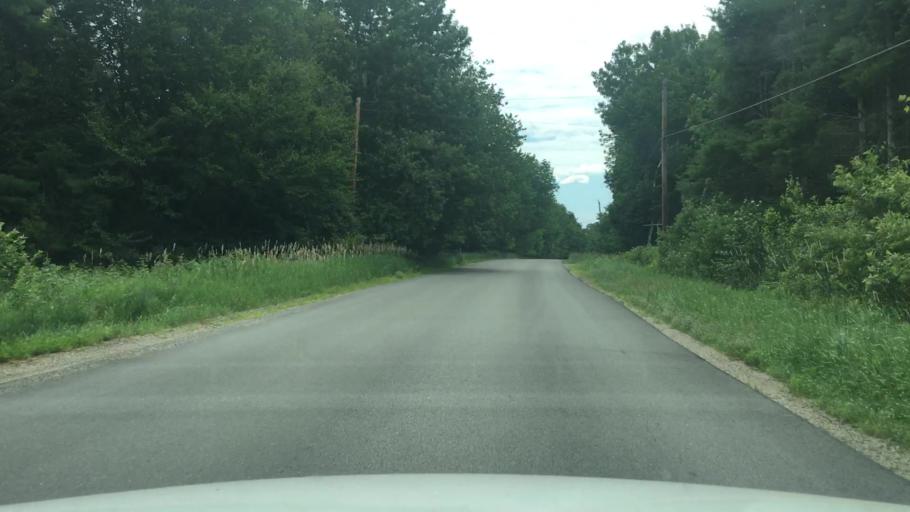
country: US
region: Maine
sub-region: Waldo County
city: Searsmont
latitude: 44.4519
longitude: -69.2523
